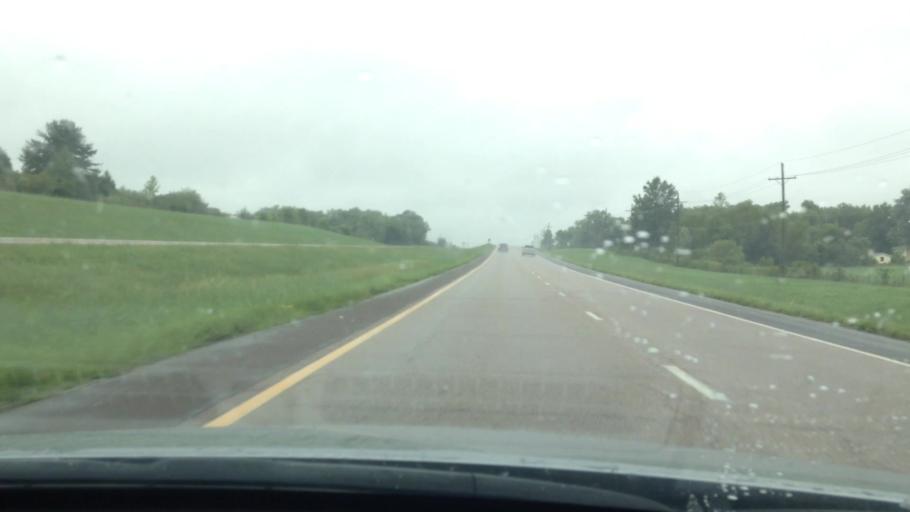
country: US
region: Kansas
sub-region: Leavenworth County
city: Lansing
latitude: 39.2101
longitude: -94.9011
